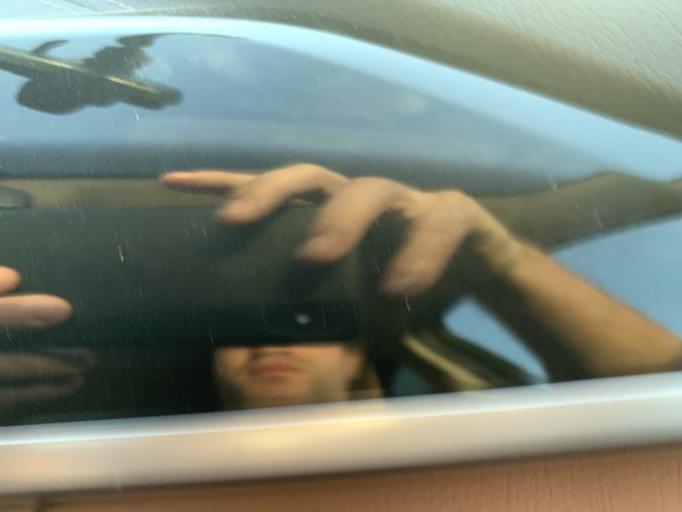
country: EG
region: Muhafazat al Qalyubiyah
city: Al Khankah
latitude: 30.0269
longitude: 31.5777
